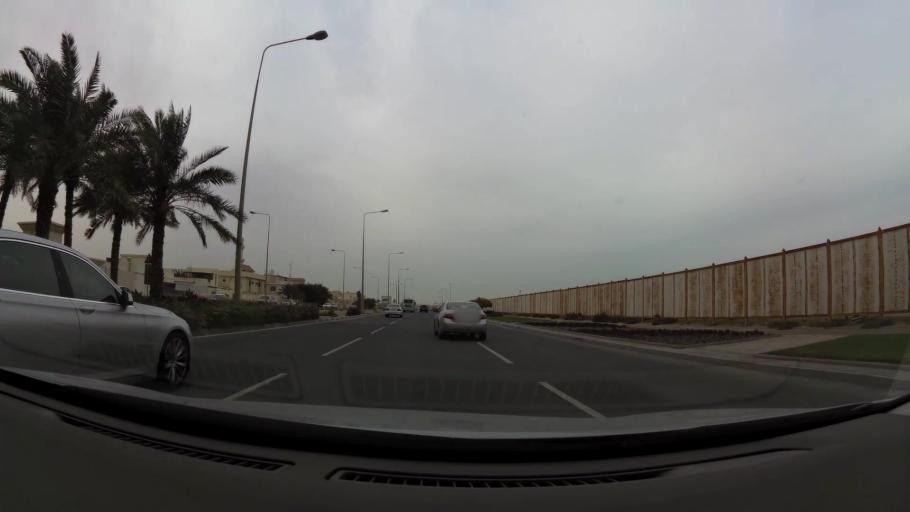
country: QA
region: Baladiyat ad Dawhah
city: Doha
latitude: 25.3178
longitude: 51.4869
